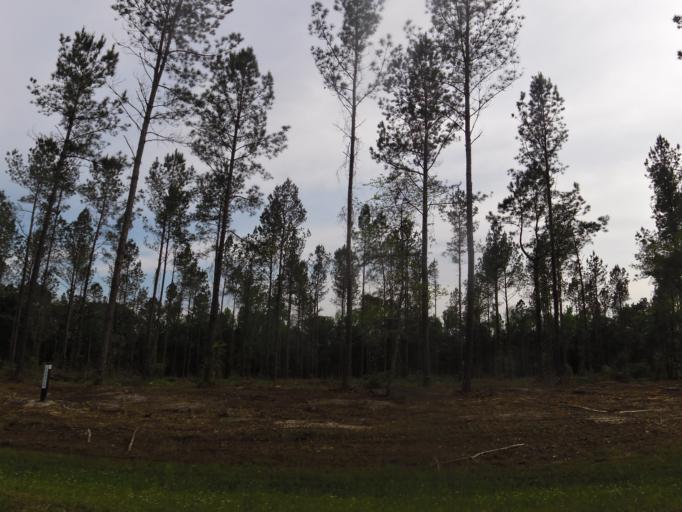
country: US
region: Georgia
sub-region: Camden County
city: Kingsland
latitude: 30.6990
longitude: -81.7706
